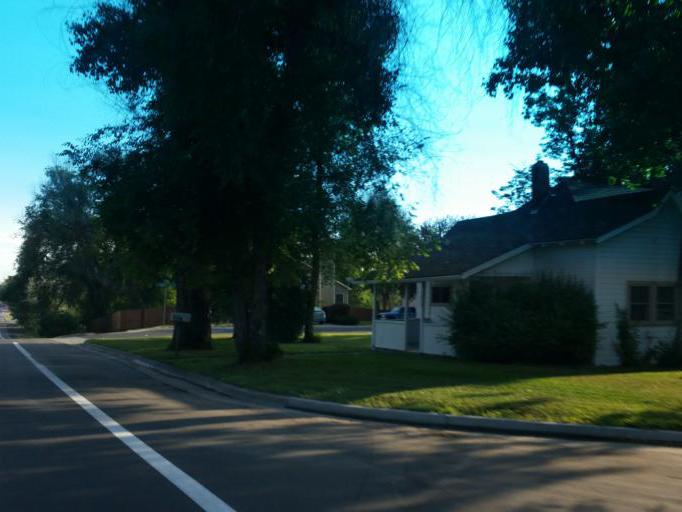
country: US
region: Colorado
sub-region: Larimer County
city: Fort Collins
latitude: 40.5630
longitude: -105.1151
